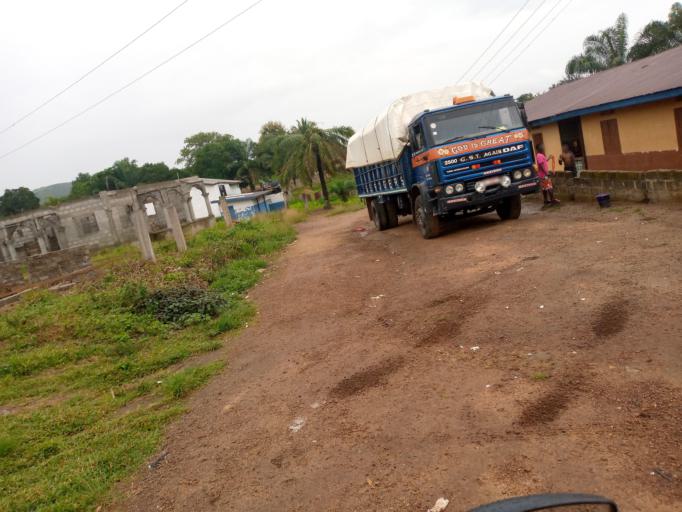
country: SL
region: Eastern Province
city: Kenema
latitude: 7.8449
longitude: -11.2038
